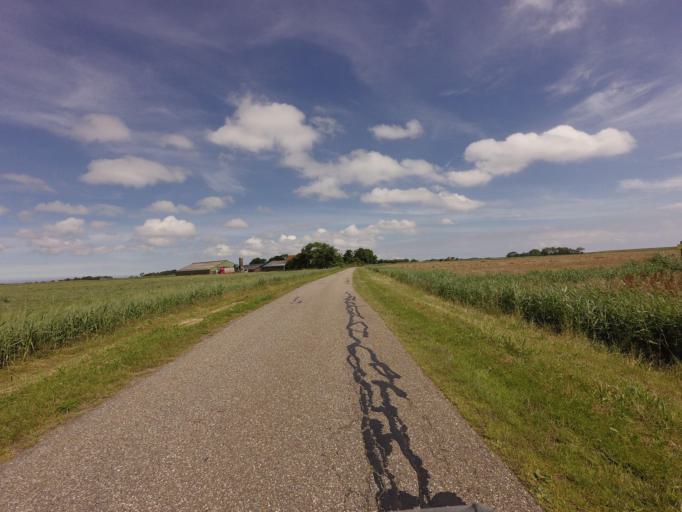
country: NL
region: North Holland
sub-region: Gemeente Texel
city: Den Burg
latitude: 53.0635
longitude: 4.8508
